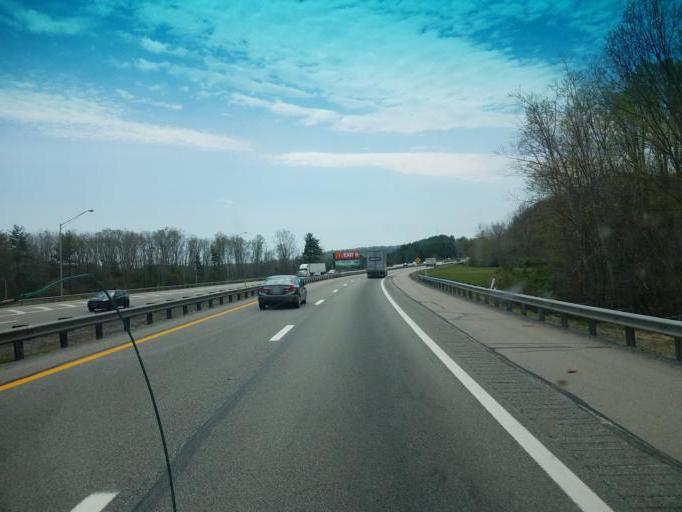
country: US
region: West Virginia
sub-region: Mercer County
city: Athens
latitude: 37.4732
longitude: -81.0682
